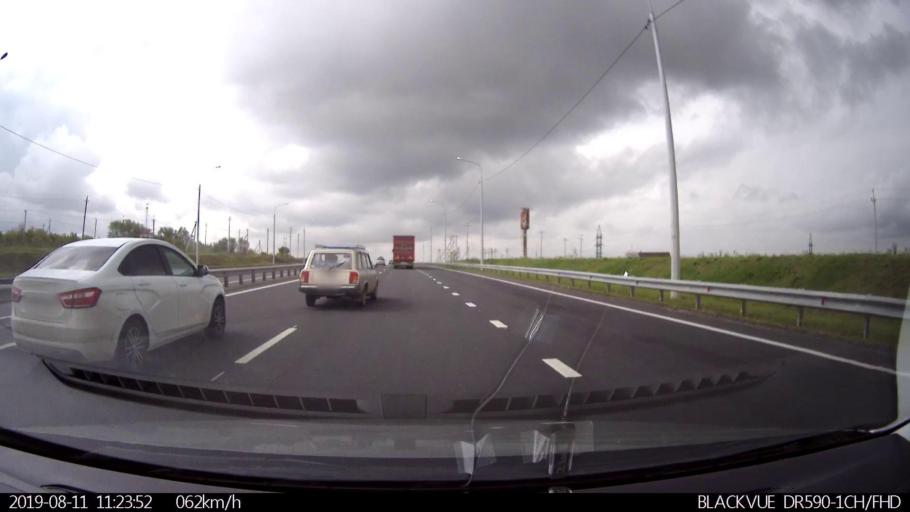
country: RU
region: Ulyanovsk
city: Krasnyy Gulyay
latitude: 54.1322
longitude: 48.2481
